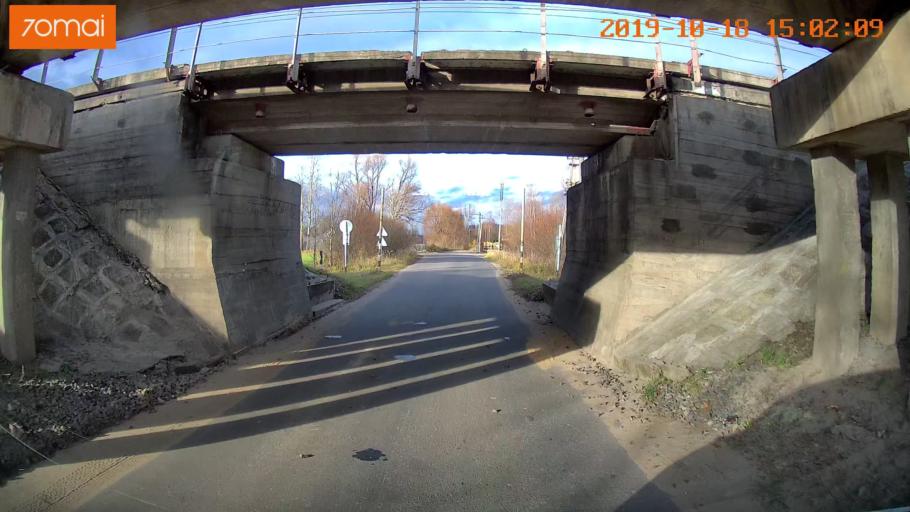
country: RU
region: Vladimir
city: Gus'-Khrustal'nyy
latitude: 55.5020
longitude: 40.6086
